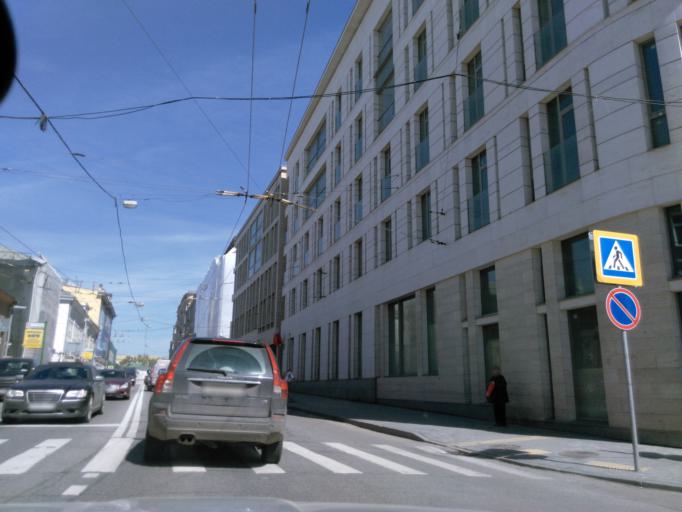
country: RU
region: Moscow
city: Moscow
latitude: 55.7417
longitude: 37.5992
